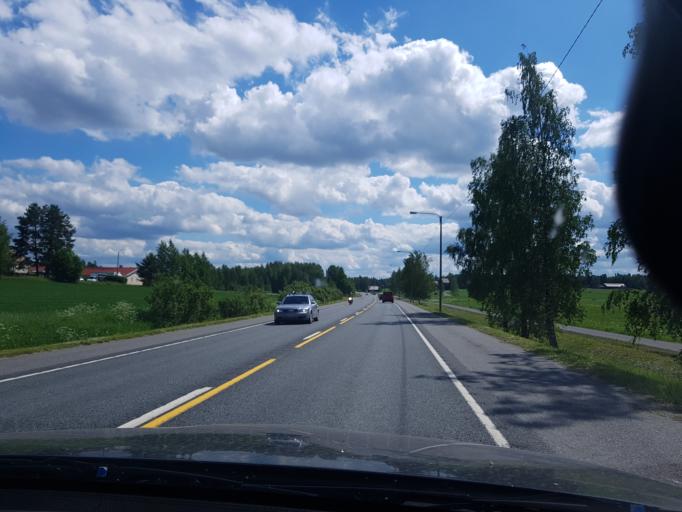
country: FI
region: Haeme
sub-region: Haemeenlinna
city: Parola
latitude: 61.0462
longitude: 24.3975
